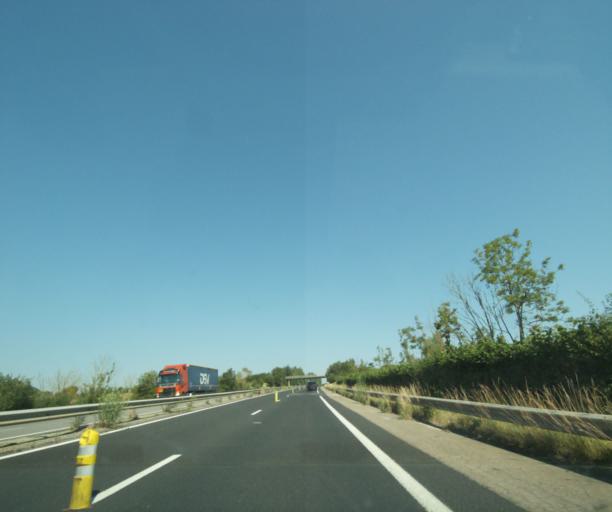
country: FR
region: Lorraine
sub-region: Departement de Meurthe-et-Moselle
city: Domgermain
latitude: 48.6549
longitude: 5.8444
